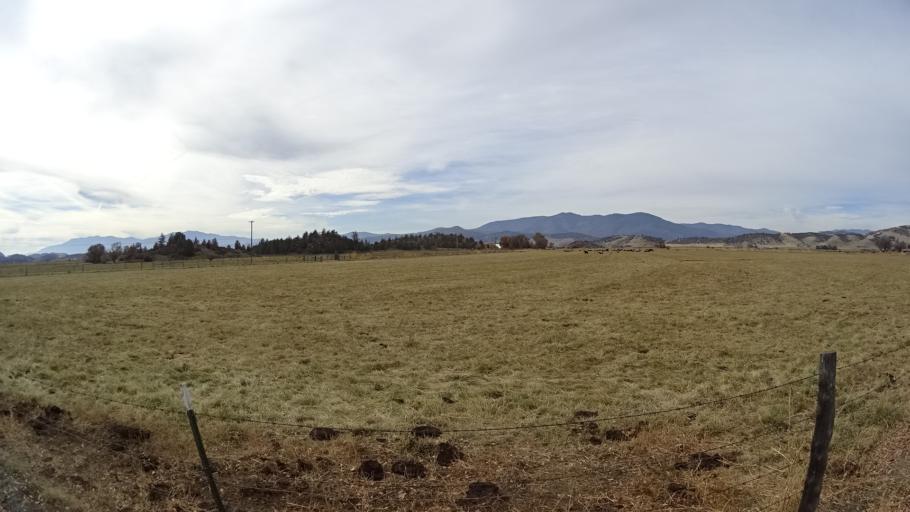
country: US
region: California
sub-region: Siskiyou County
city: Montague
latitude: 41.6629
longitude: -122.5025
